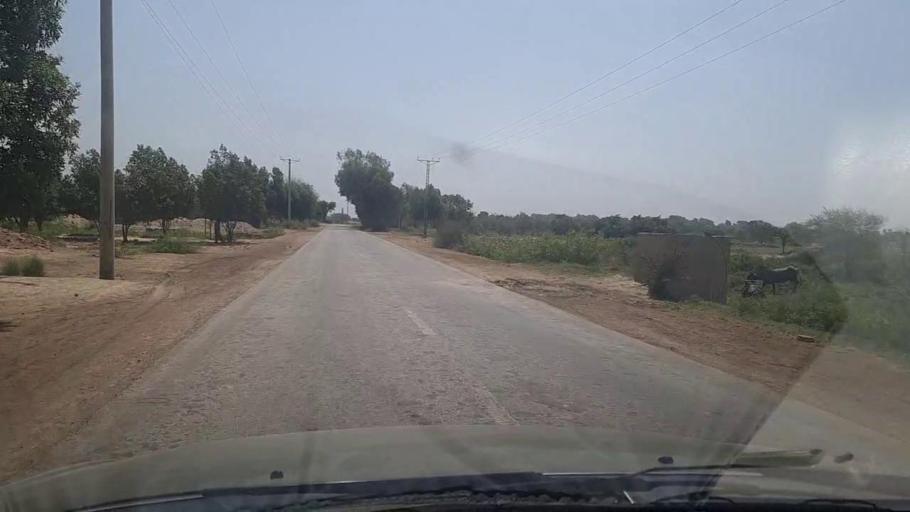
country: PK
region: Sindh
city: Hyderabad
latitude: 25.3801
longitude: 68.4522
